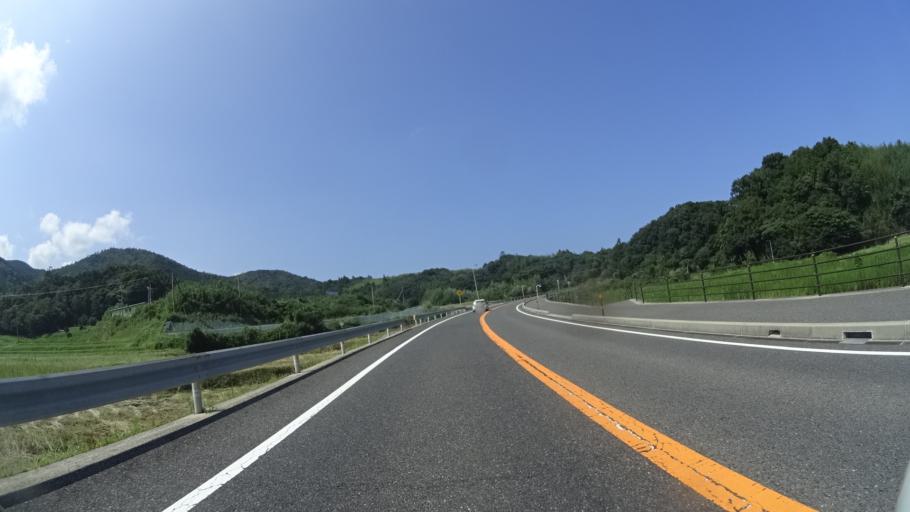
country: JP
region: Shimane
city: Masuda
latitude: 34.6707
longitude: 131.7324
